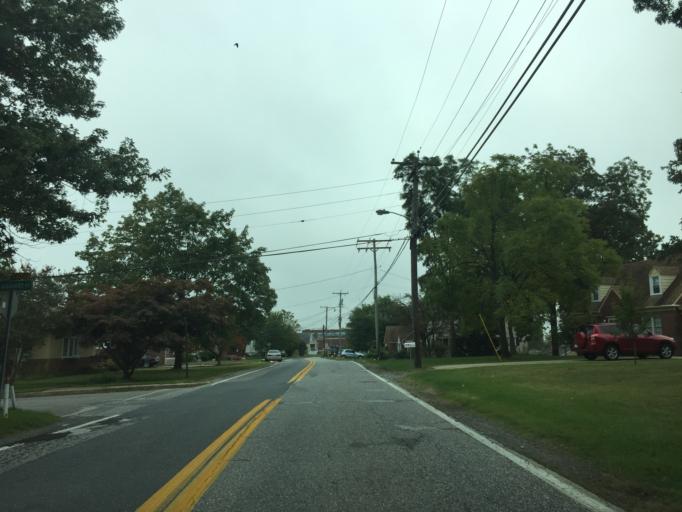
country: US
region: Maryland
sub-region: Baltimore County
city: Rosedale
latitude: 39.3347
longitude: -76.5017
